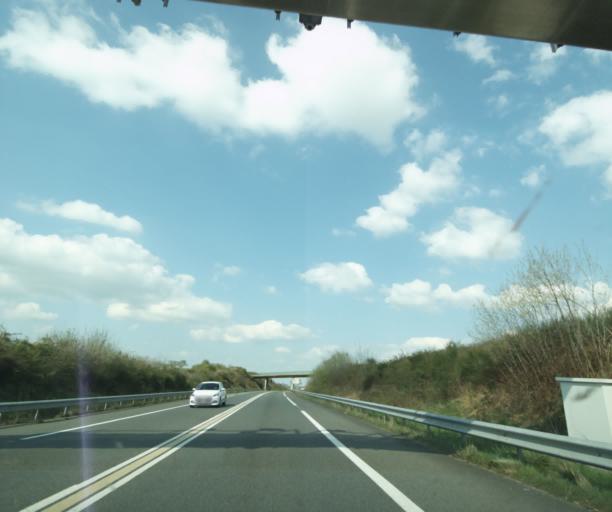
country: FR
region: Auvergne
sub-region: Departement de l'Allier
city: Montmarault
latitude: 46.3901
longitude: 3.0334
